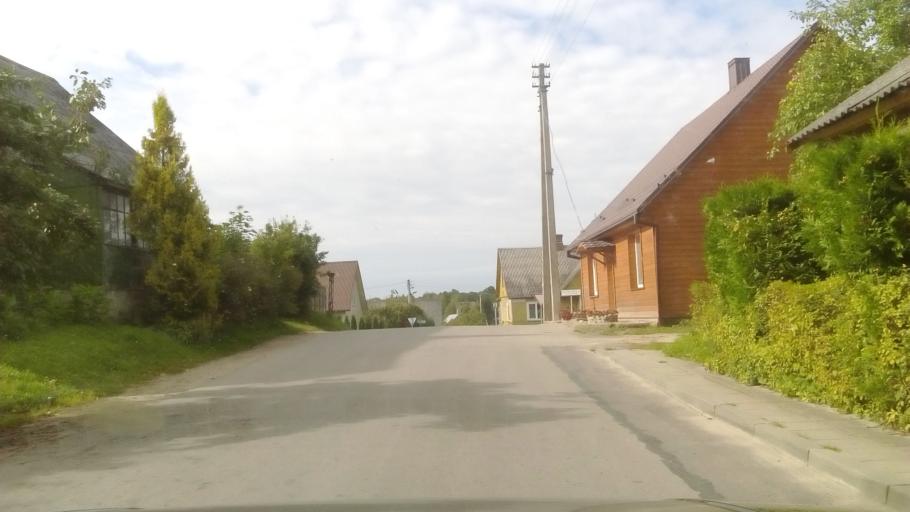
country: LT
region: Alytaus apskritis
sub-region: Alytus
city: Alytus
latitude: 54.3320
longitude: 23.8976
